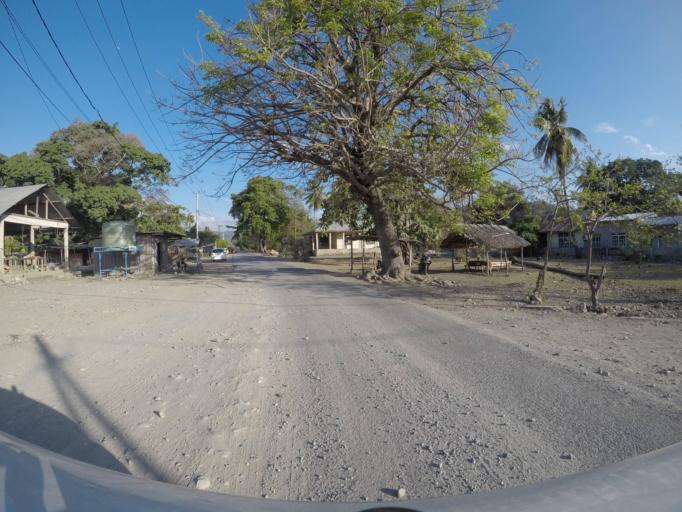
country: ID
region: East Nusa Tenggara
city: Atambua
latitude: -8.9470
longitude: 124.9732
